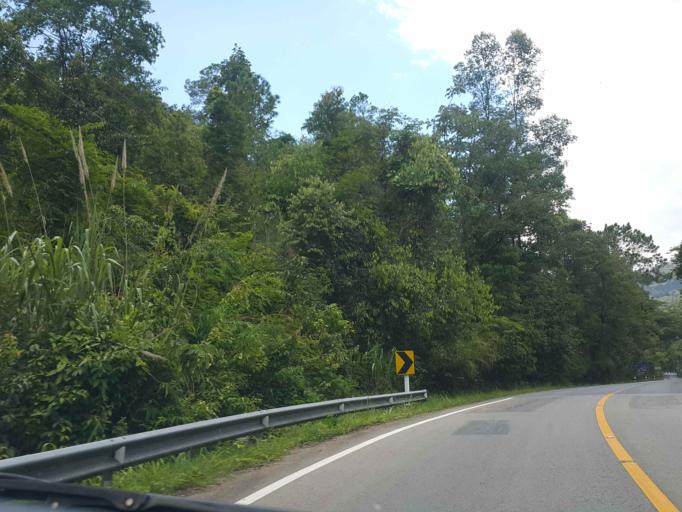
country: TH
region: Chiang Mai
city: Chom Thong
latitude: 18.5410
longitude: 98.5947
